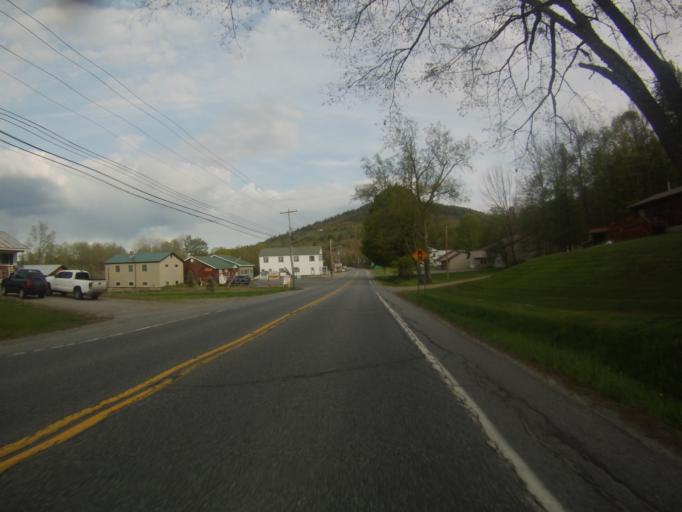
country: US
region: New York
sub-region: Warren County
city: Warrensburg
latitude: 43.6351
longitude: -73.9429
